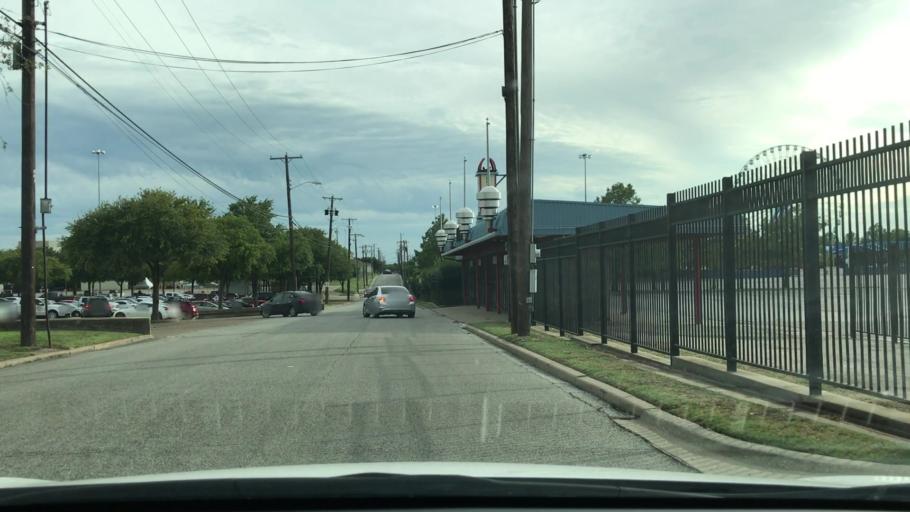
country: US
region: Texas
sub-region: Dallas County
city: Dallas
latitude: 32.7784
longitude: -96.7544
